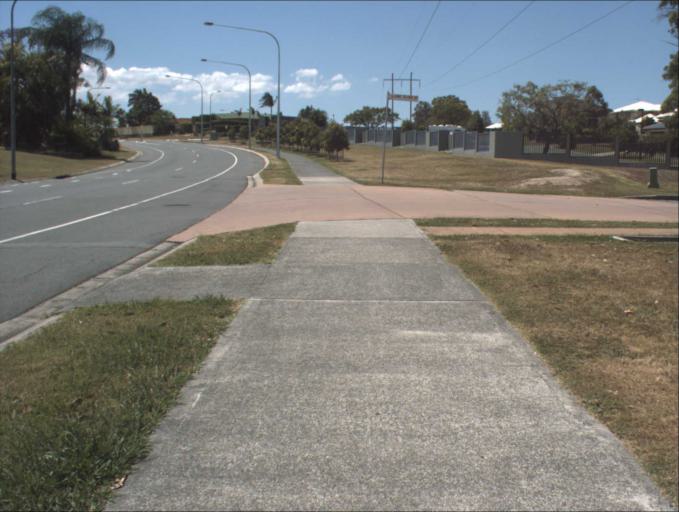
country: AU
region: Queensland
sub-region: Logan
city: Windaroo
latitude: -27.7434
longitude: 153.1928
